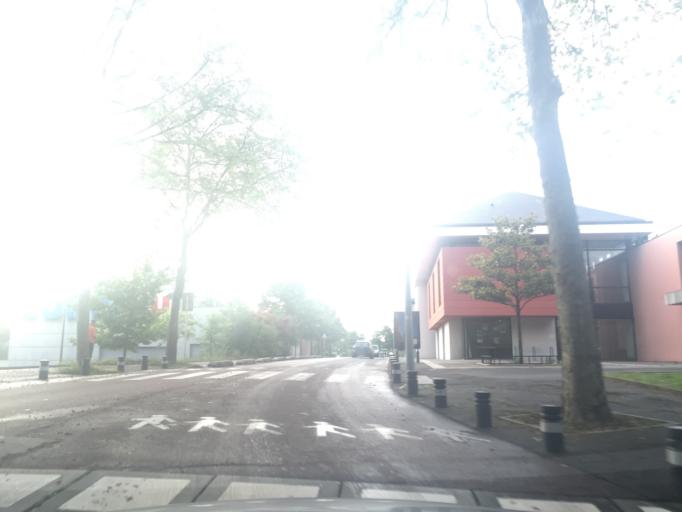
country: FR
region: Rhone-Alpes
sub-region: Departement de la Savoie
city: Bassens
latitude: 45.5898
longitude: 5.9205
